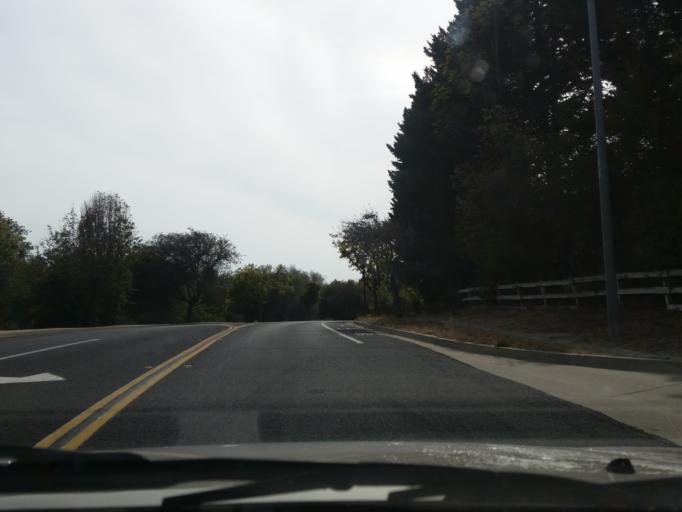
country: US
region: California
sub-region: San Luis Obispo County
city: Arroyo Grande
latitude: 35.1341
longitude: -120.5965
